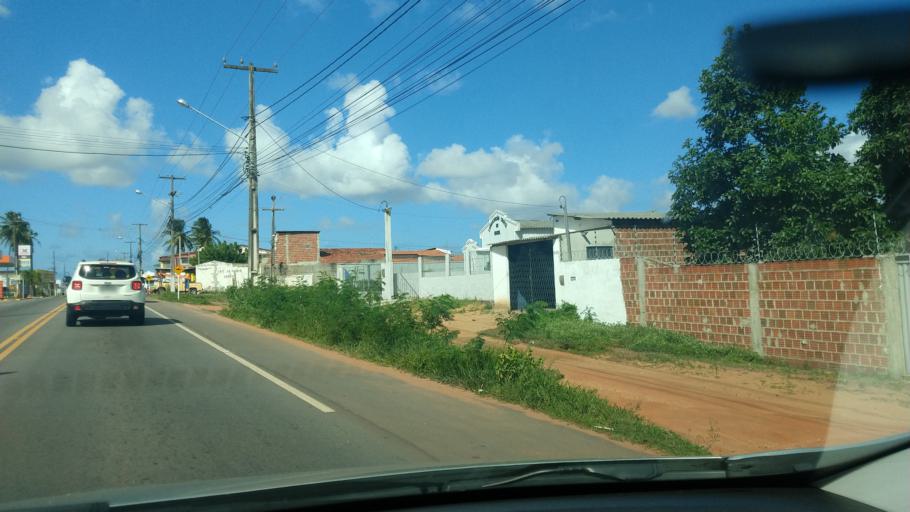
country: BR
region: Rio Grande do Norte
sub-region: Sao Goncalo Do Amarante
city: Sao Goncalo do Amarante
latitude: -5.7887
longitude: -35.3005
